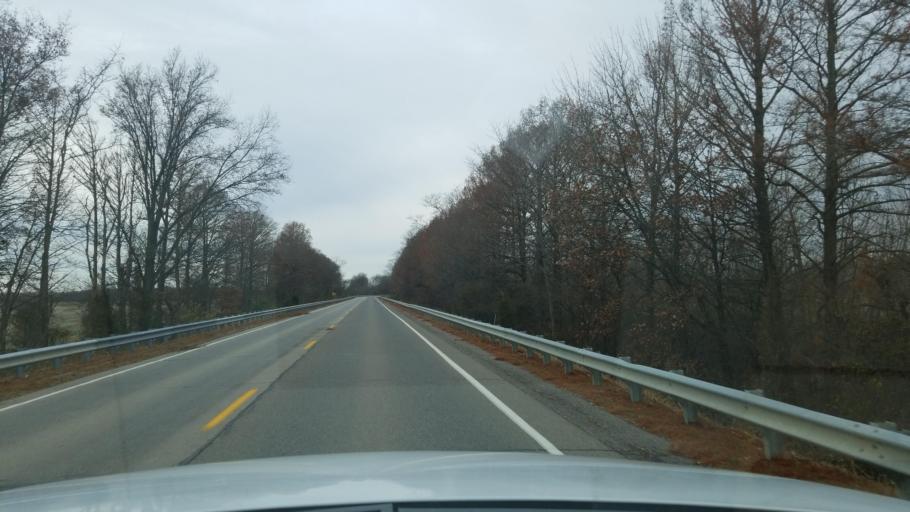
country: US
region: Indiana
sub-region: Posey County
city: Mount Vernon
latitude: 37.9290
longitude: -87.9922
